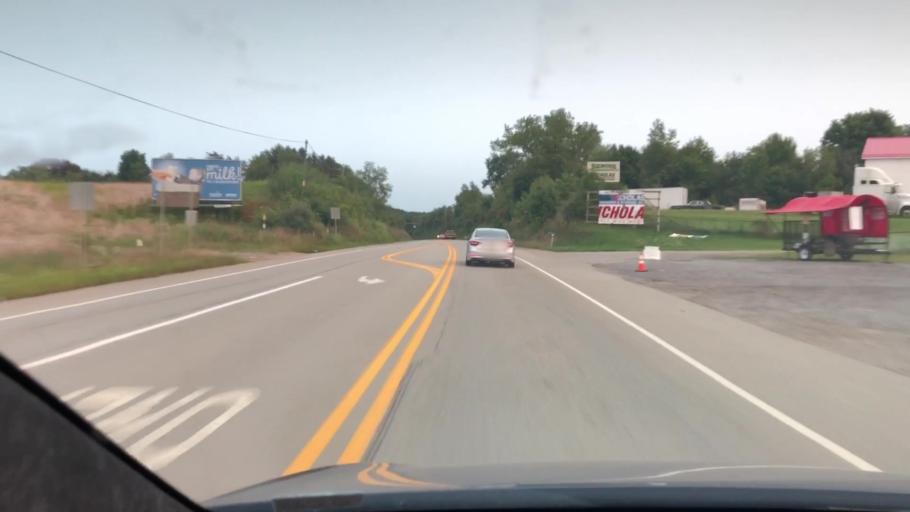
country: US
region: Pennsylvania
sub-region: Butler County
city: Shanor-Northvue
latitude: 40.9201
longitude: -79.9468
